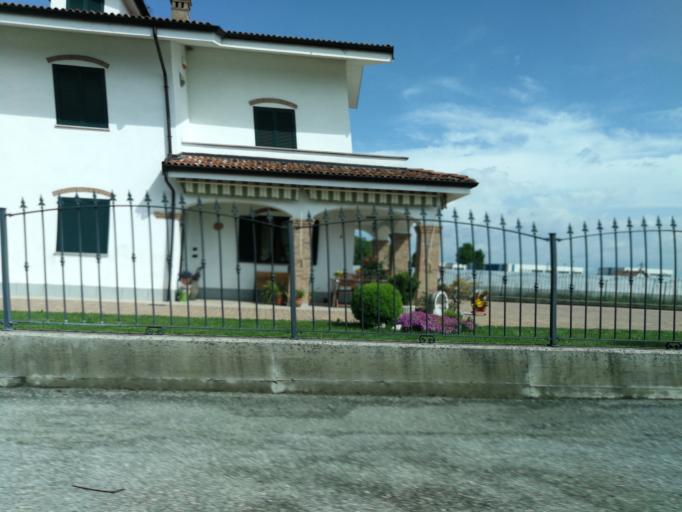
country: IT
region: Piedmont
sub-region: Provincia di Cuneo
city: Faule
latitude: 44.8027
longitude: 7.5781
